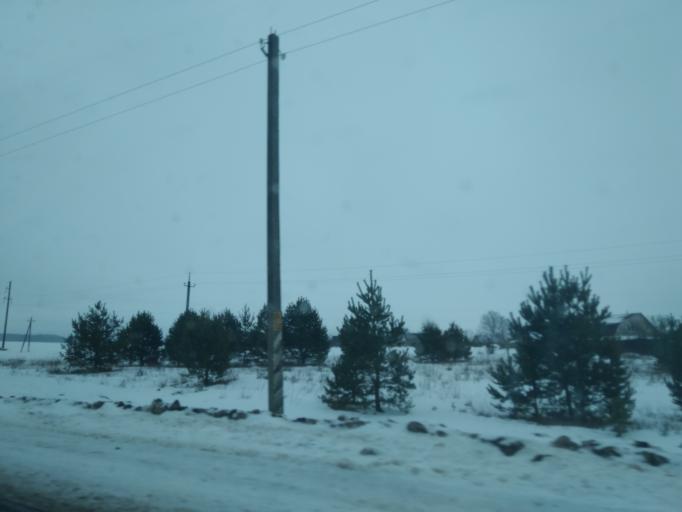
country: BY
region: Minsk
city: Stowbtsy
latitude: 53.5691
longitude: 26.7968
